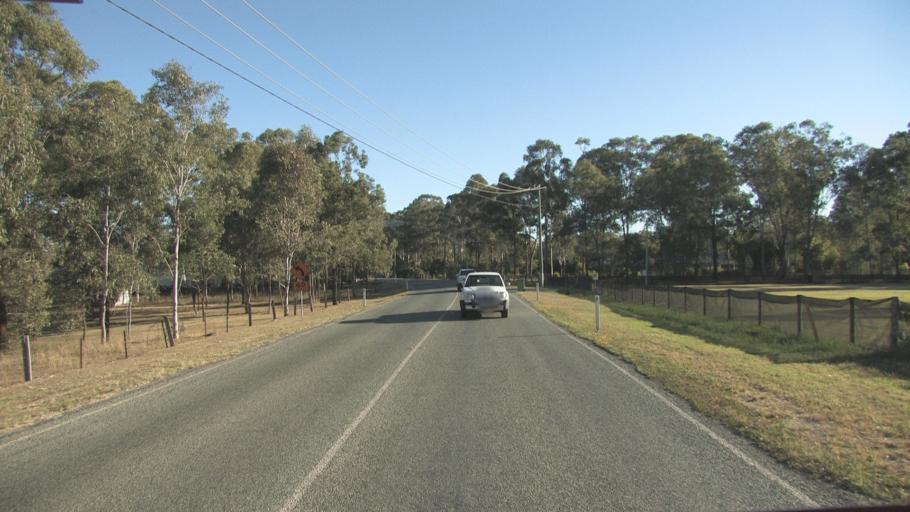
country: AU
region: Queensland
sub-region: Logan
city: Chambers Flat
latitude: -27.7465
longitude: 153.0607
